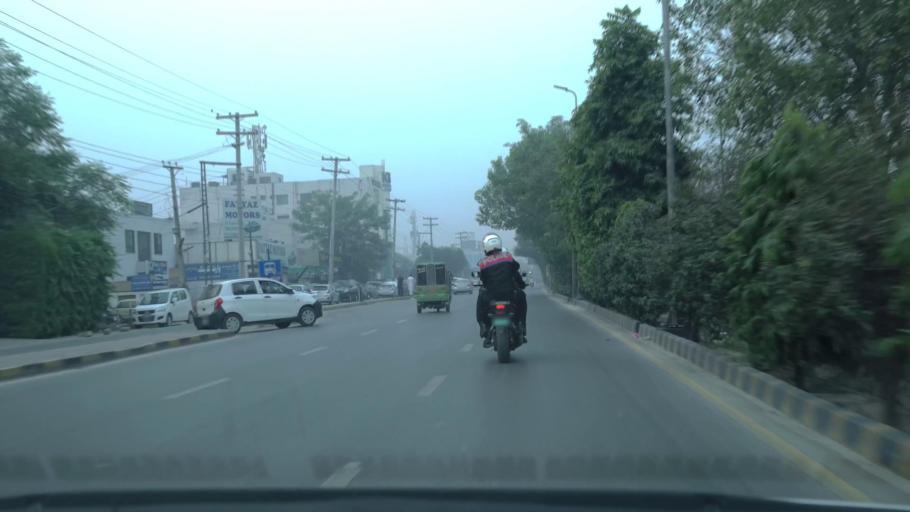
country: PK
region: Punjab
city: Lahore
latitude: 31.4753
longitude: 74.3018
